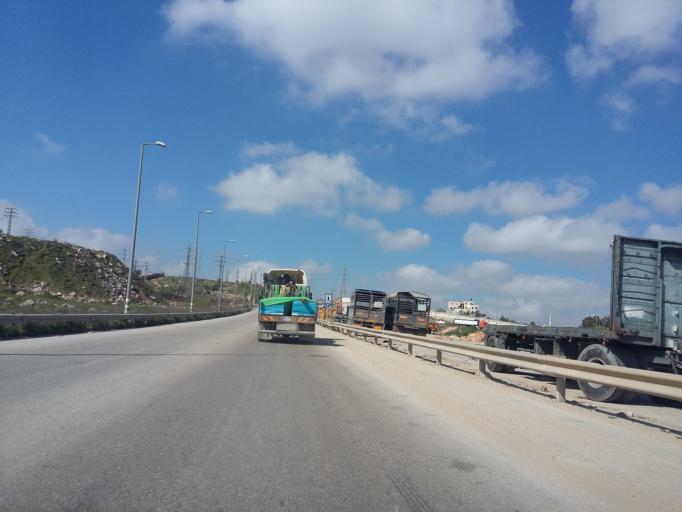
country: PS
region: West Bank
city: Qalandiya
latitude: 31.8605
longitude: 35.2182
